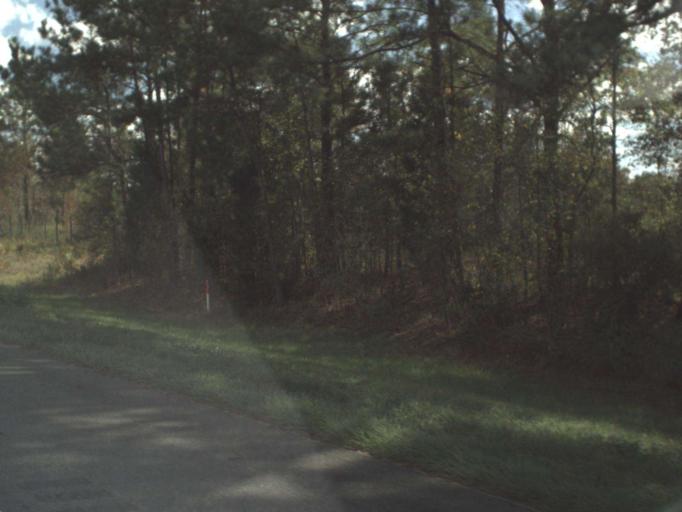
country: US
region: Florida
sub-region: Jackson County
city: Marianna
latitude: 30.7457
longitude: -85.2571
